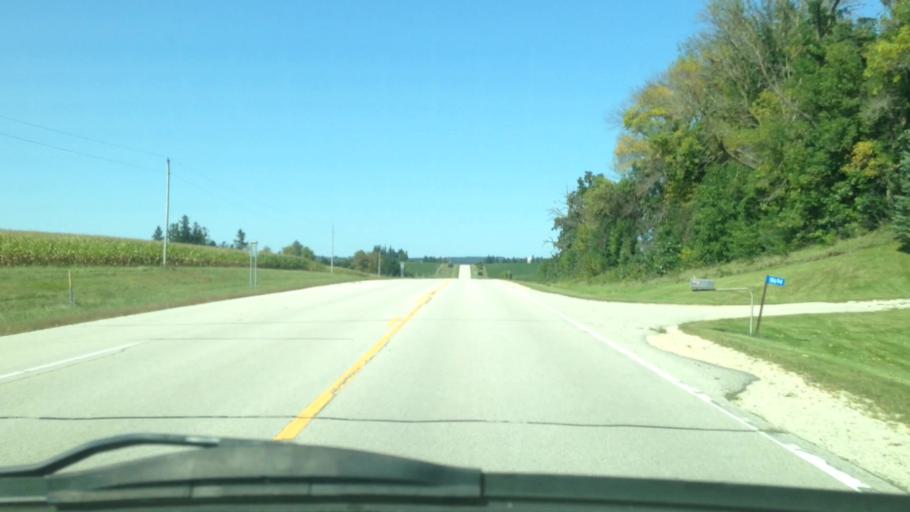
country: US
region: Minnesota
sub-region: Houston County
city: Spring Grove
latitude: 43.6277
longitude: -91.7903
